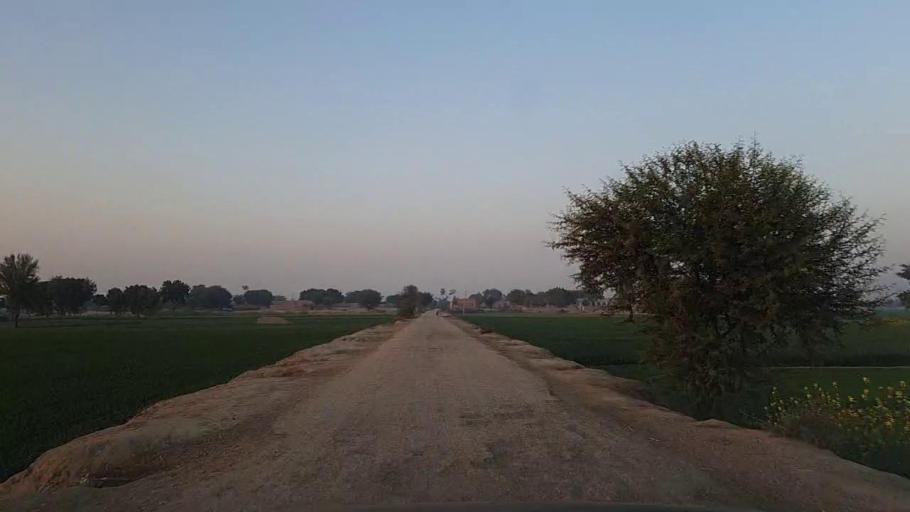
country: PK
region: Sindh
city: Jam Sahib
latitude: 26.4676
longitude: 68.5420
